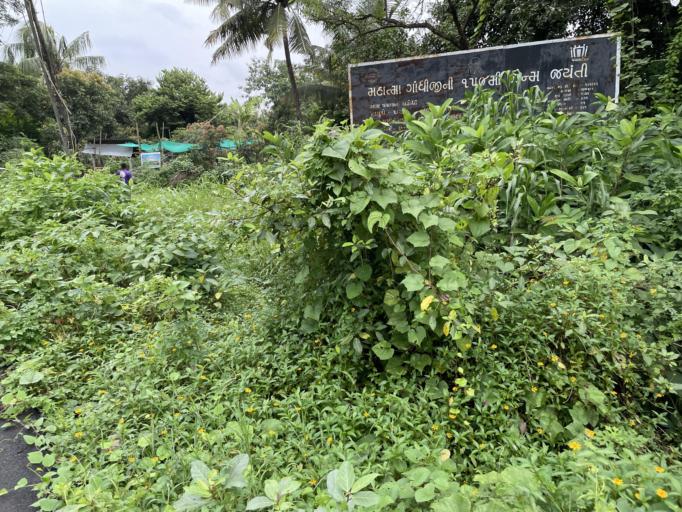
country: IN
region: Gujarat
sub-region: Valsad
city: Pardi
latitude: 20.4526
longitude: 72.9344
